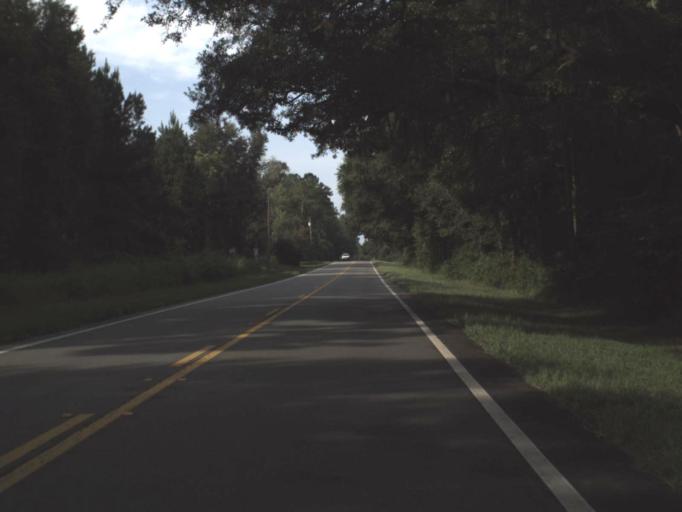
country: US
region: Florida
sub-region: Madison County
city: Madison
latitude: 30.3980
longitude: -83.6537
